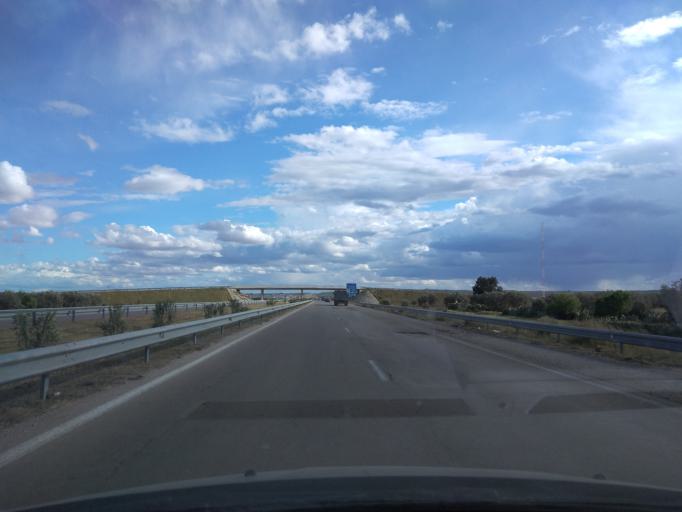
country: TN
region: Al Munastir
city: Manzil Kamil
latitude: 35.5838
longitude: 10.6074
